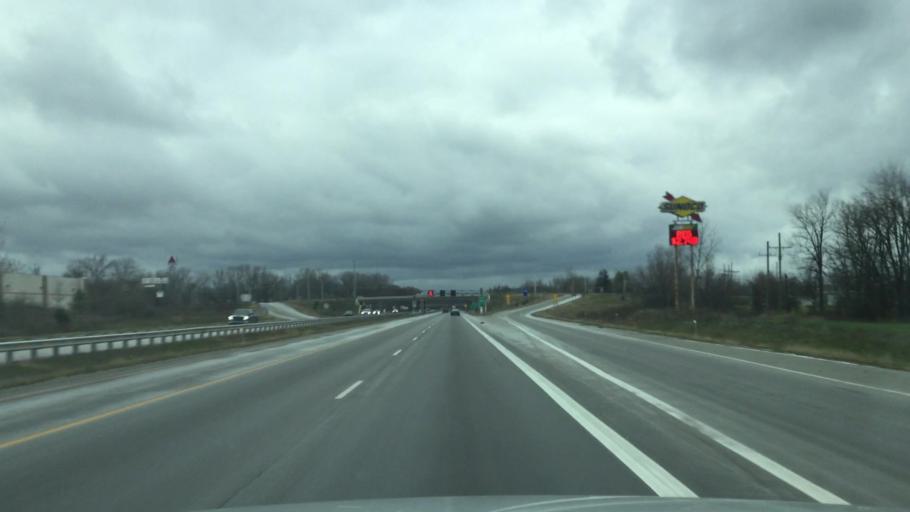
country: US
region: Michigan
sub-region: Livingston County
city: Whitmore Lake
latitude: 42.3765
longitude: -83.7551
